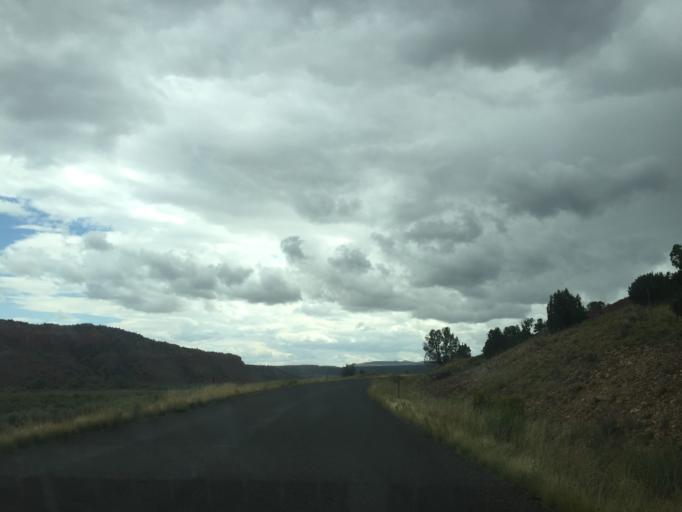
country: US
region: Utah
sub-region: Garfield County
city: Panguitch
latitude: 37.5447
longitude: -112.0446
